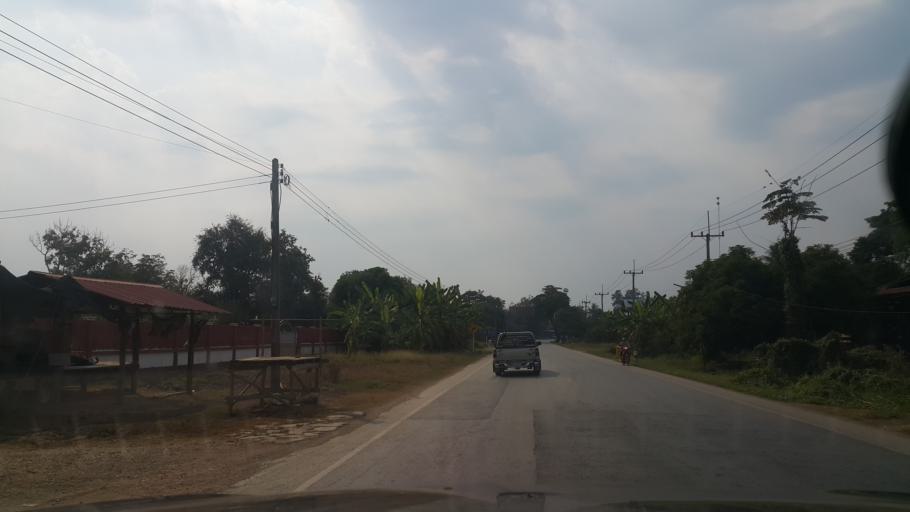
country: TH
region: Sukhothai
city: Si Samrong
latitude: 17.0912
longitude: 99.8836
